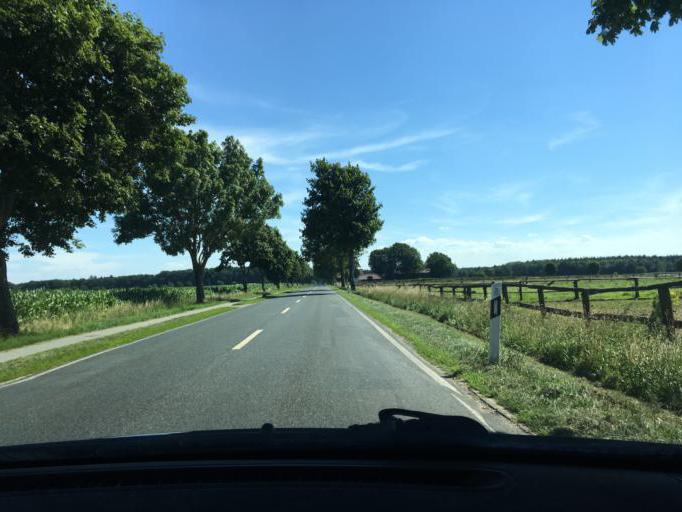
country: DE
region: Lower Saxony
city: Bendestorf
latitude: 53.3626
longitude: 9.9420
